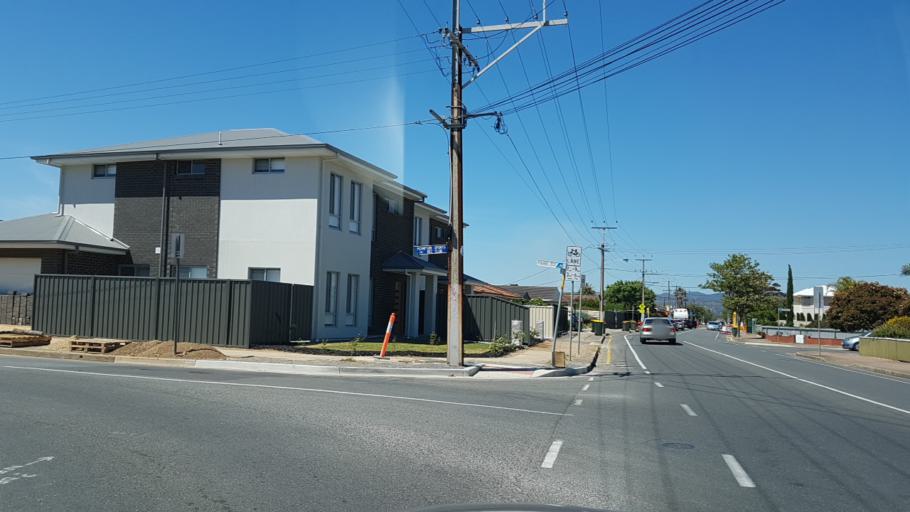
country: AU
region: South Australia
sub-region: Marion
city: Plympton Park
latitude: -34.9809
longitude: 138.5471
